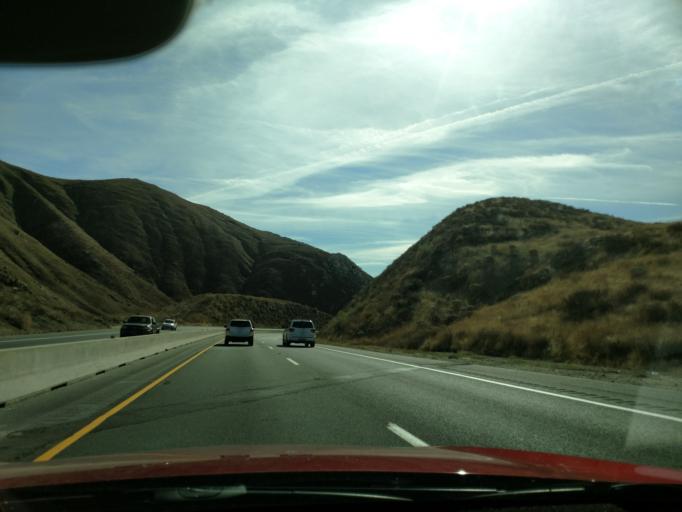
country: US
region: California
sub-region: Riverside County
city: Beaumont
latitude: 33.8642
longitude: -117.0083
